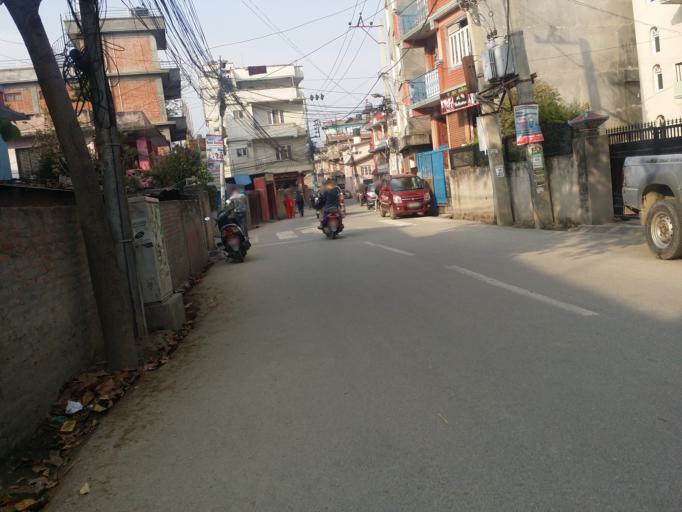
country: NP
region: Central Region
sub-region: Bagmati Zone
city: Kathmandu
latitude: 27.7007
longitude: 85.3460
